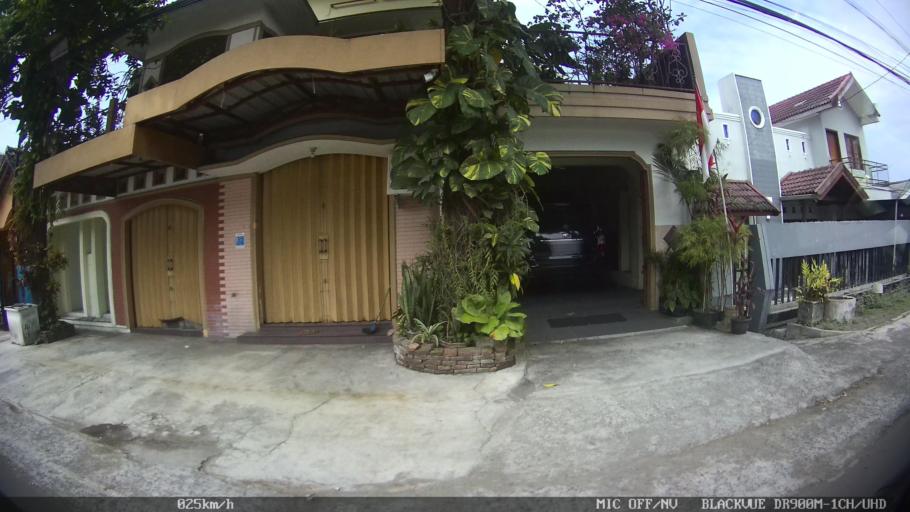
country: ID
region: Daerah Istimewa Yogyakarta
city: Depok
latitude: -7.7519
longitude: 110.4486
